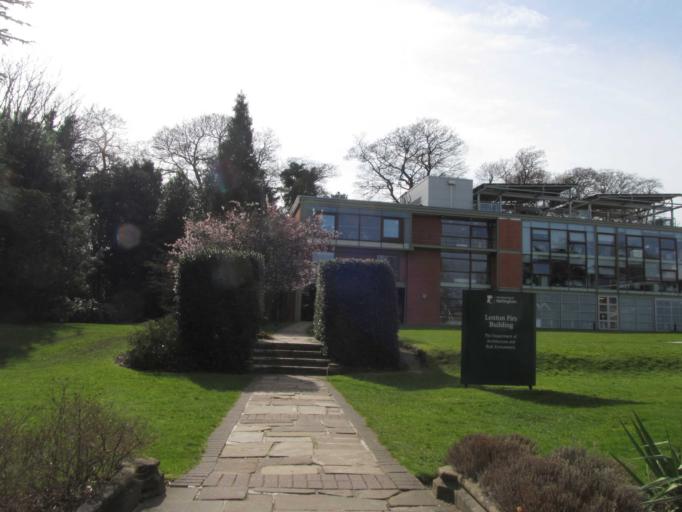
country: GB
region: England
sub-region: Nottingham
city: Nottingham
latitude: 52.9441
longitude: -1.1944
